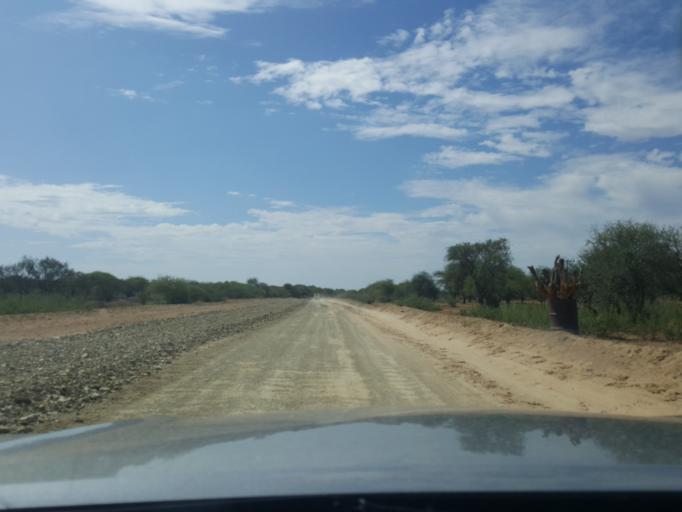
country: BW
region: Kweneng
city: Letlhakeng
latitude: -23.9820
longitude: 24.9673
